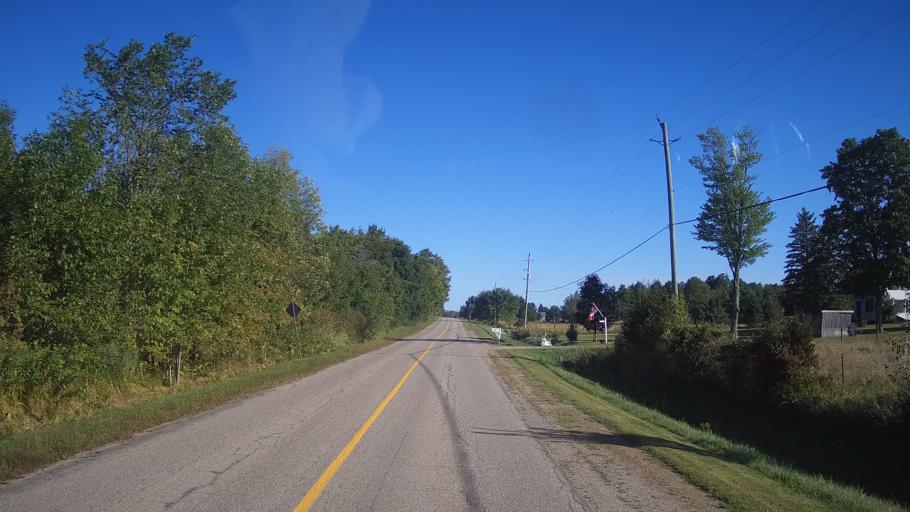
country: US
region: New York
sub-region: Jefferson County
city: Alexandria Bay
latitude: 44.4589
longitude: -75.9872
